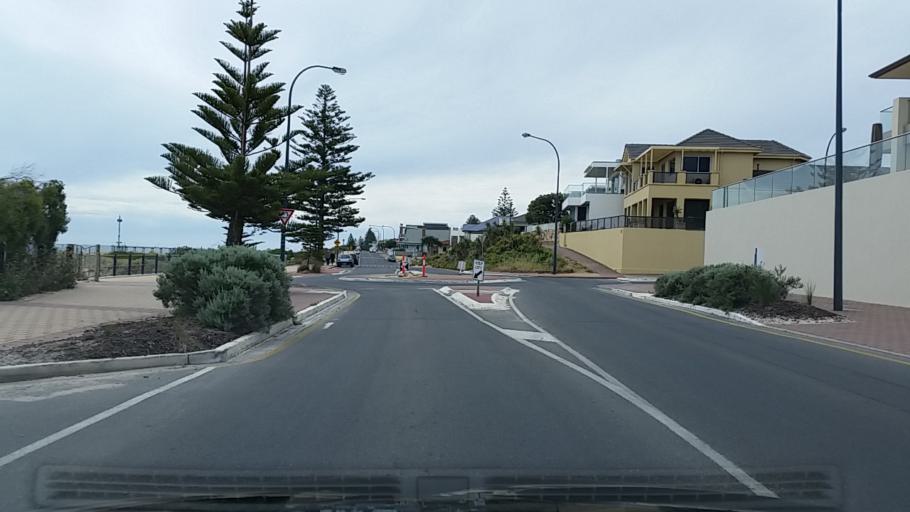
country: AU
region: South Australia
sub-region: Adelaide
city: Brighton
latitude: -35.0234
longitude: 138.5167
